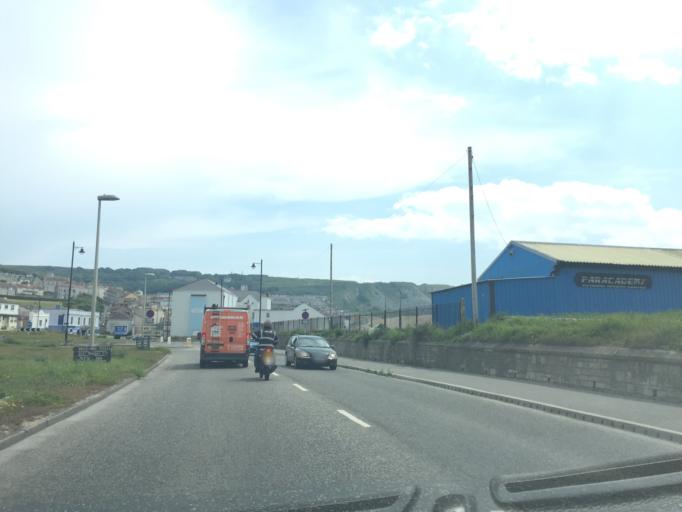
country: GB
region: England
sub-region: Dorset
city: Portland
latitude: 50.5642
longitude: -2.4515
